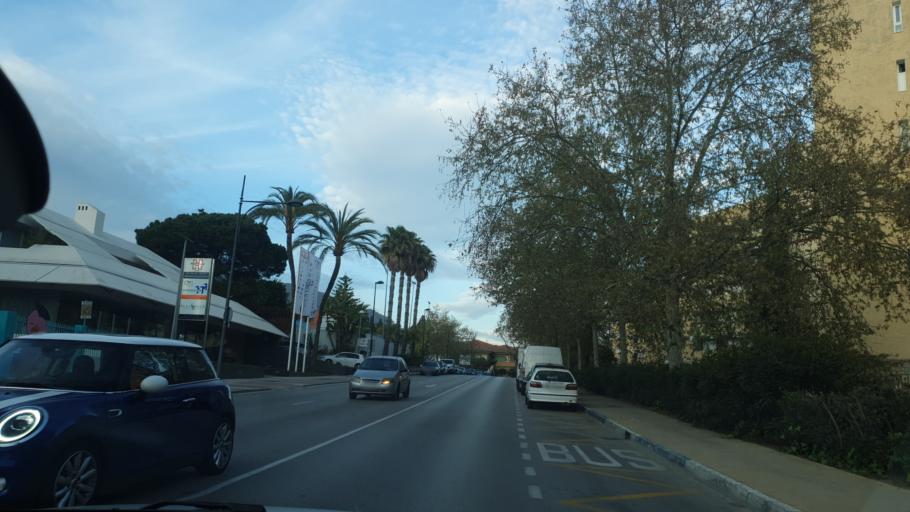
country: ES
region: Andalusia
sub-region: Provincia de Malaga
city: Marbella
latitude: 36.5154
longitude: -4.8957
